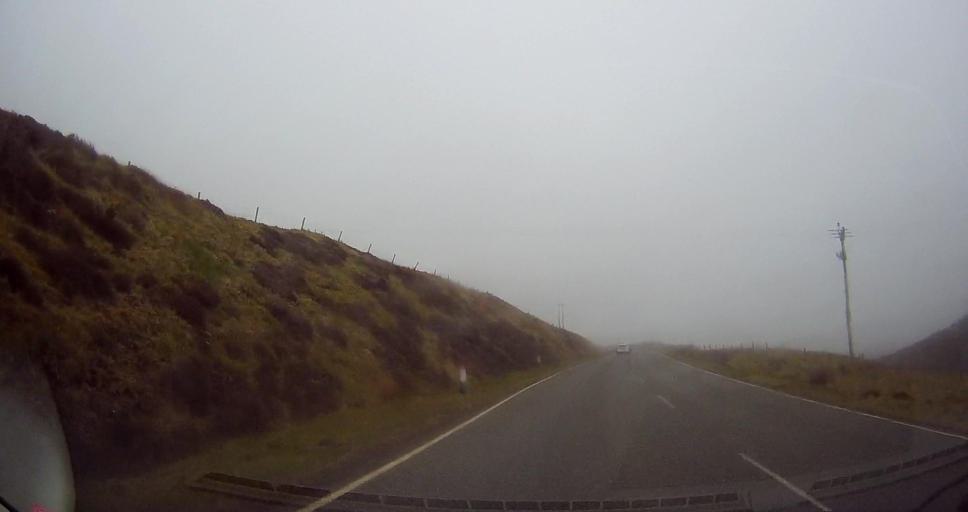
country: GB
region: Scotland
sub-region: Shetland Islands
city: Lerwick
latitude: 60.1404
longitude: -1.2364
